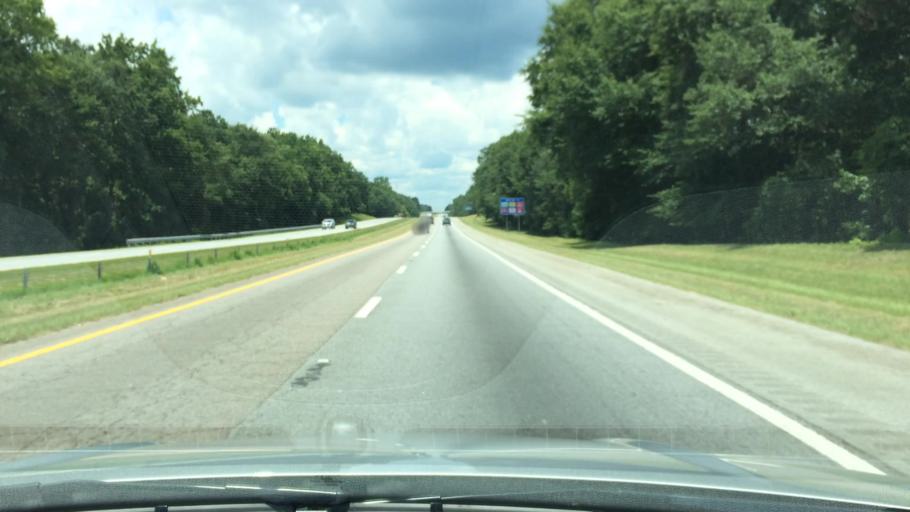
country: US
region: South Carolina
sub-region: Newberry County
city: Newberry
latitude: 34.3034
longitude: -81.5607
